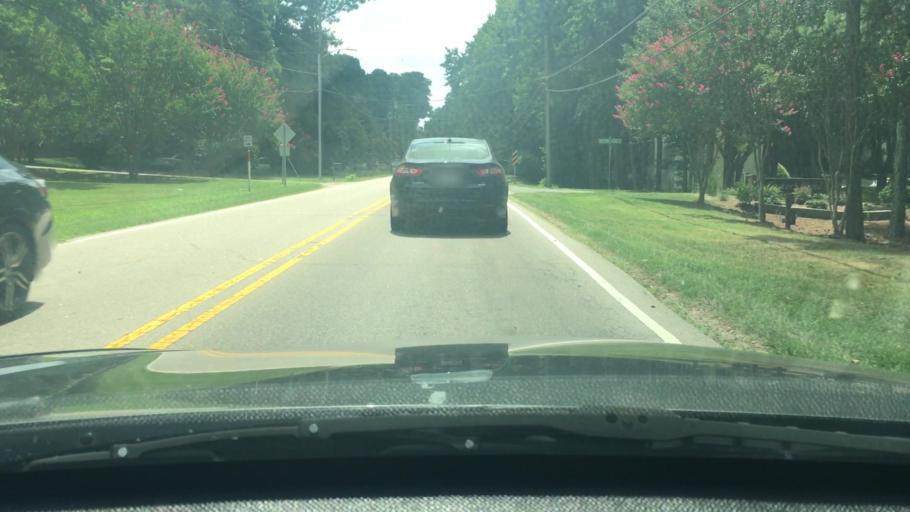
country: US
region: North Carolina
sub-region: Wake County
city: Cary
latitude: 35.7948
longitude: -78.7917
